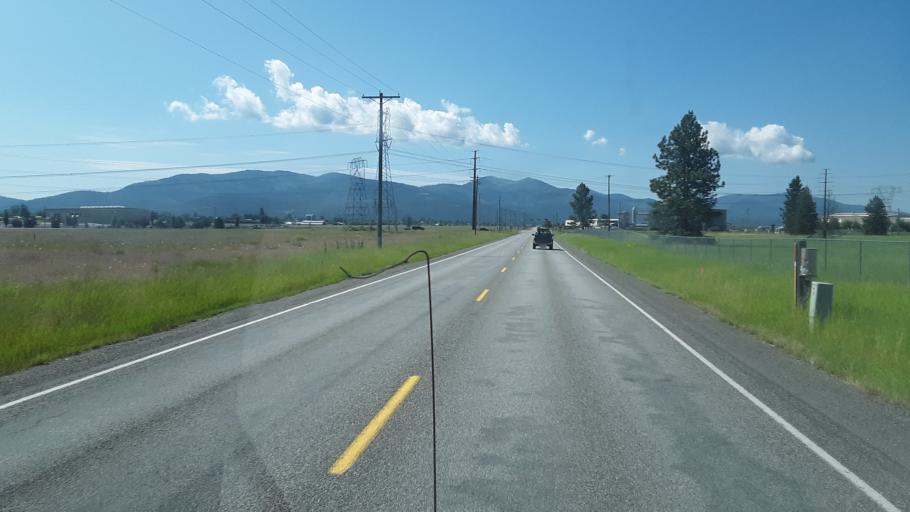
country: US
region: Idaho
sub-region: Kootenai County
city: Post Falls
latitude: 47.7483
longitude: -117.0021
